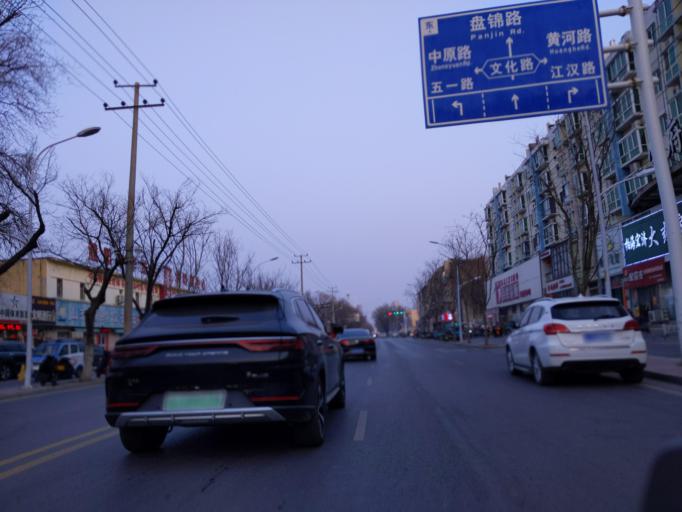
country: CN
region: Henan Sheng
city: Zhongyuanlu
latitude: 35.7700
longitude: 115.0899
